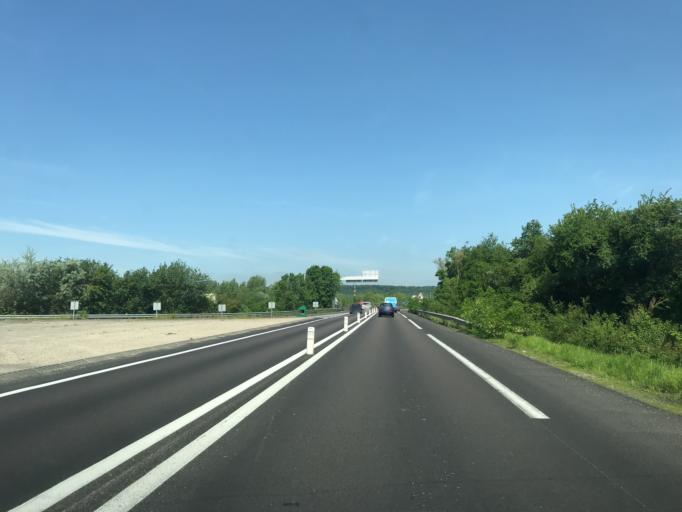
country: FR
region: Haute-Normandie
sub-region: Departement de la Seine-Maritime
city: Oissel
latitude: 49.3249
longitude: 1.0918
